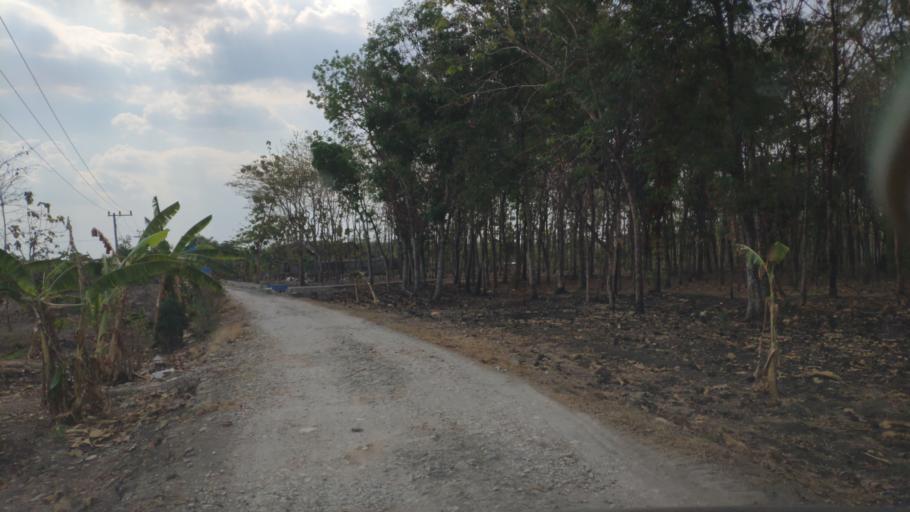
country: ID
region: Central Java
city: Mendenrejo
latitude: -7.3119
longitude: 111.3643
